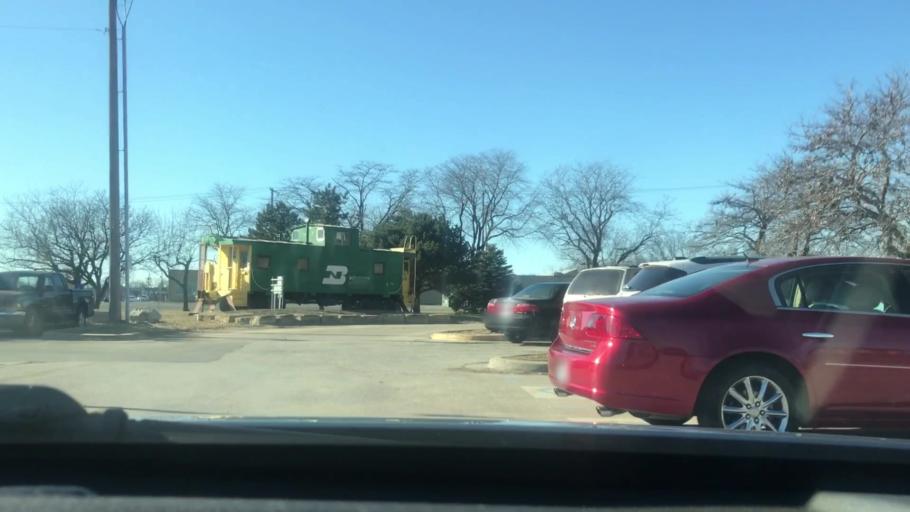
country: US
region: Missouri
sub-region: Clay County
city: North Kansas City
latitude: 39.1418
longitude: -94.5717
